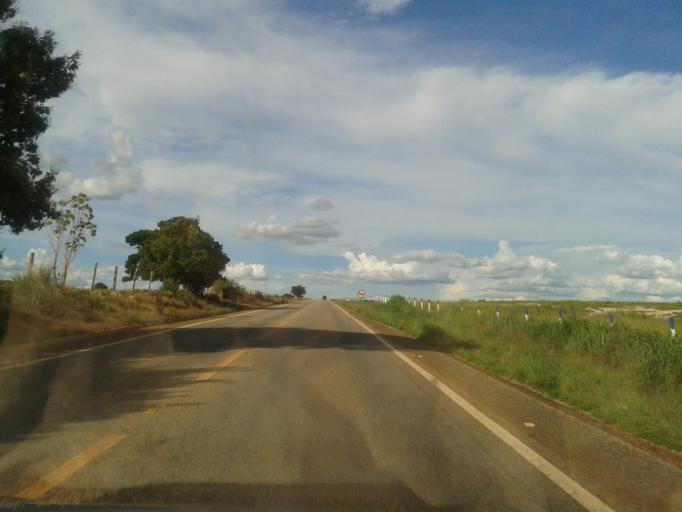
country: BR
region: Goias
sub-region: Mozarlandia
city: Mozarlandia
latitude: -14.3421
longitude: -50.4188
